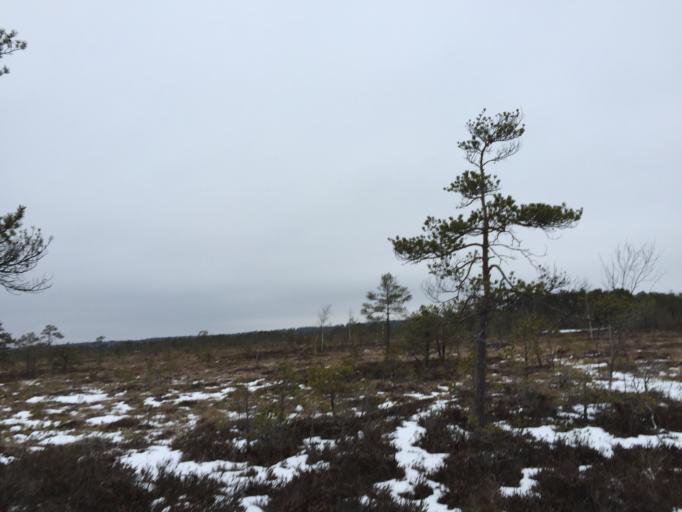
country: LV
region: Saulkrastu
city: Saulkrasti
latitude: 57.2320
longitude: 24.5042
